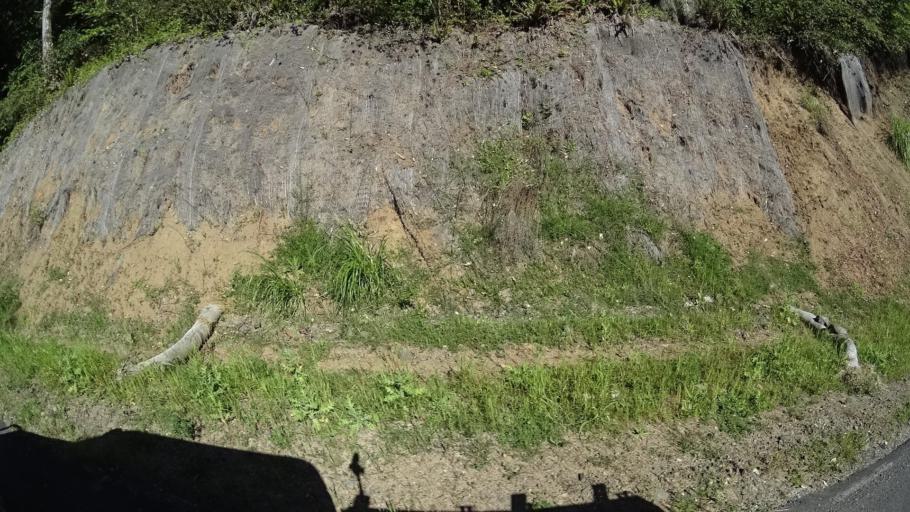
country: US
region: California
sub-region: Humboldt County
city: Rio Dell
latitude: 40.4558
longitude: -124.0210
